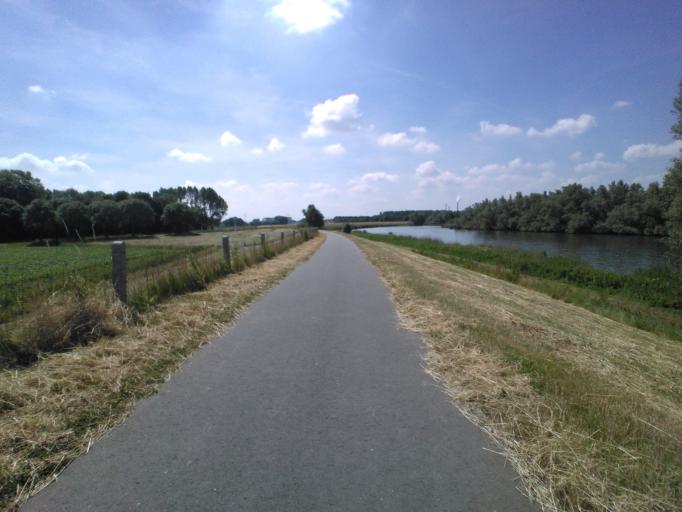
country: NL
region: North Brabant
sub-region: Gemeente Geertruidenberg
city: Geertruidenberg
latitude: 51.7537
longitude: 4.8531
